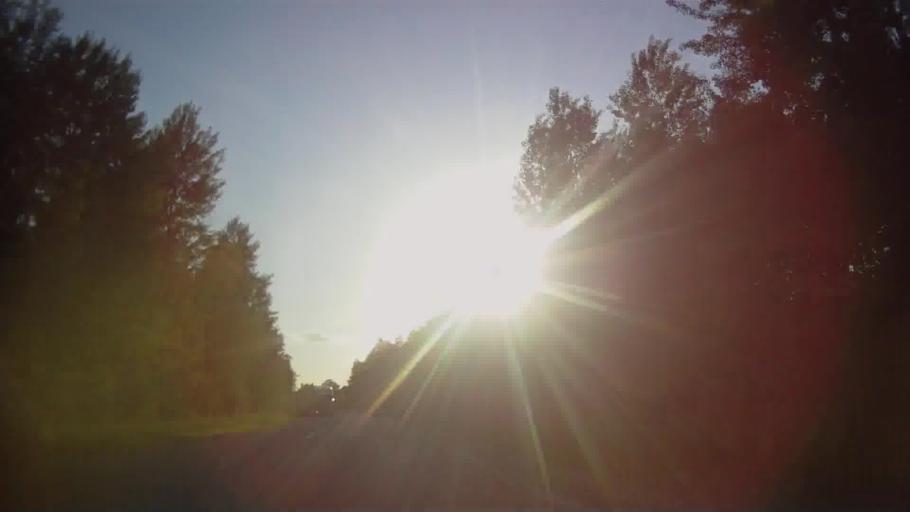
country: LV
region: Livani
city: Livani
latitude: 56.5284
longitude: 26.3953
